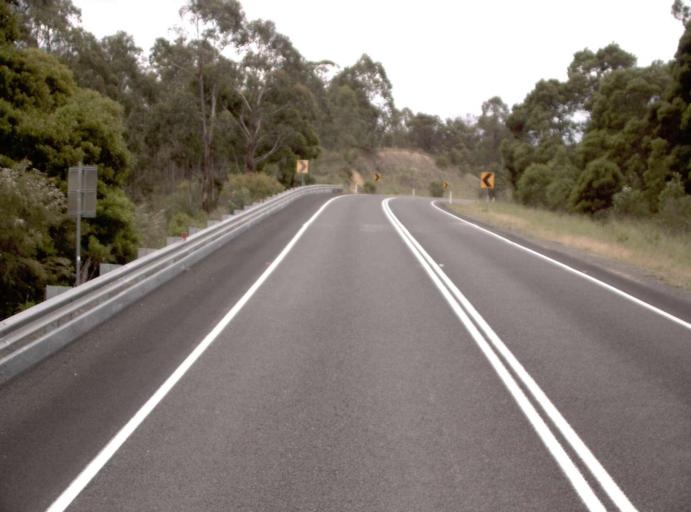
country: AU
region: New South Wales
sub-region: Bombala
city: Bombala
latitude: -37.2450
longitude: 149.2590
